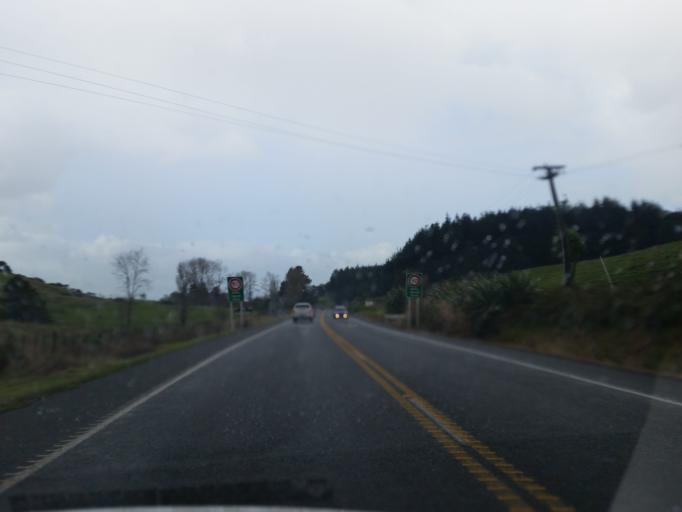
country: NZ
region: Waikato
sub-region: Hauraki District
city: Ngatea
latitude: -37.2787
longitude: 175.3284
